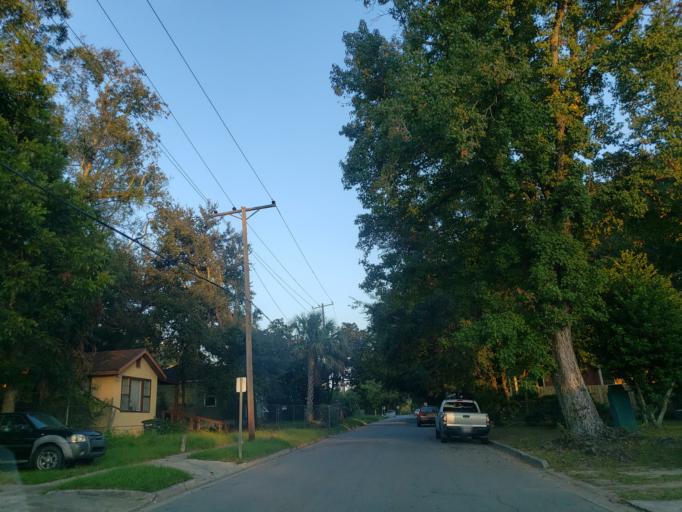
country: US
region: Georgia
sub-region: Chatham County
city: Savannah
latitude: 32.0611
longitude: -81.0763
